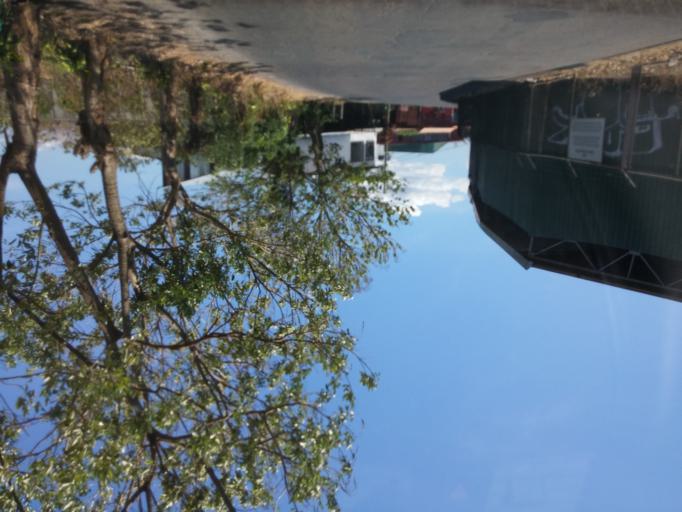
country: CR
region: Alajuela
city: Alajuela
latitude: 10.0154
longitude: -84.2292
